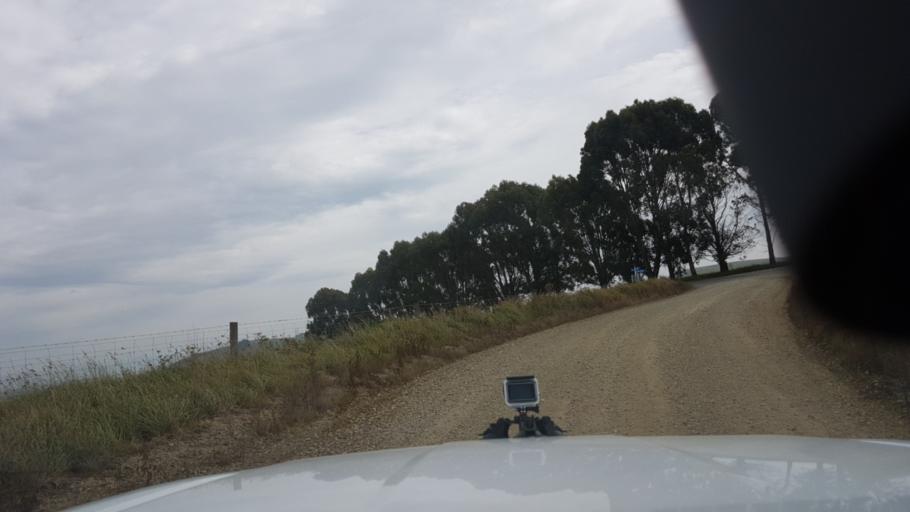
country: NZ
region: Otago
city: Oamaru
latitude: -45.0334
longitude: 170.9664
